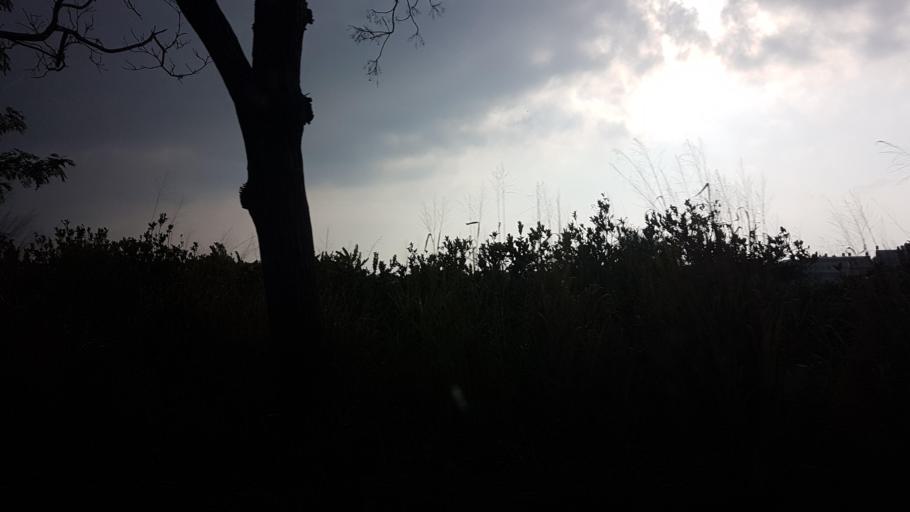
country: TW
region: Taiwan
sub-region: Chiayi
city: Jiayi Shi
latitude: 23.3780
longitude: 120.4524
